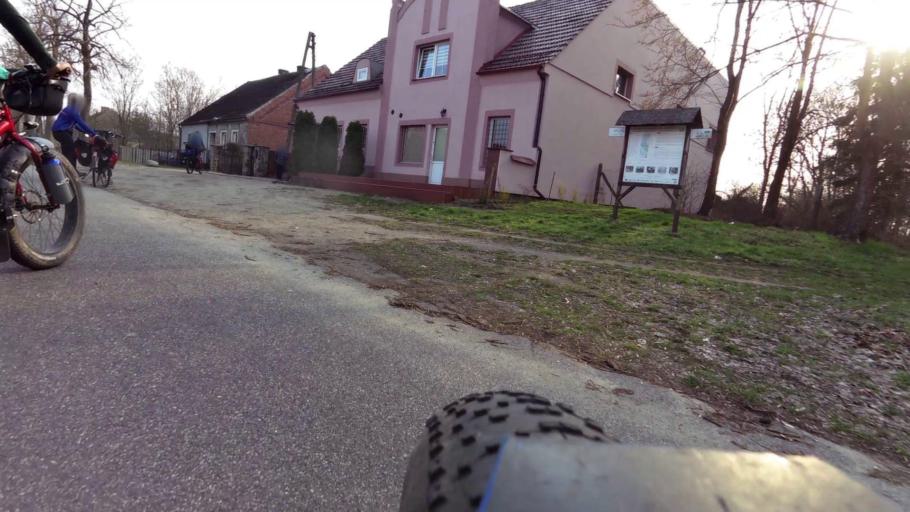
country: DE
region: Brandenburg
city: Vogelsang
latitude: 52.2459
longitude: 14.7079
